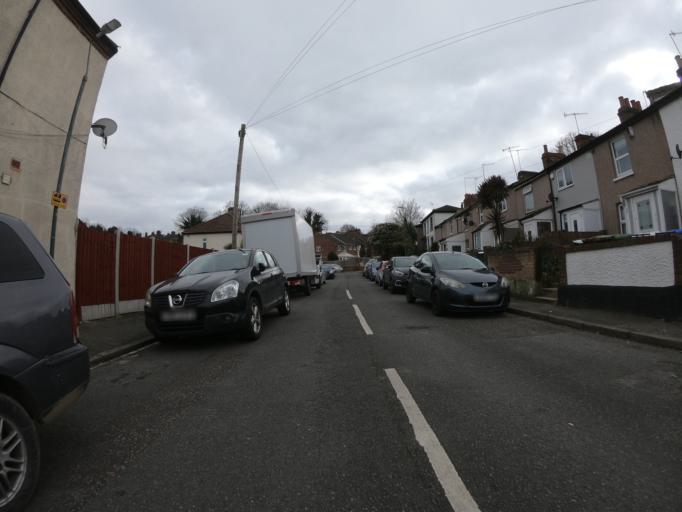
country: GB
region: England
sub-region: Greater London
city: Belvedere
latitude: 51.4885
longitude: 0.1476
